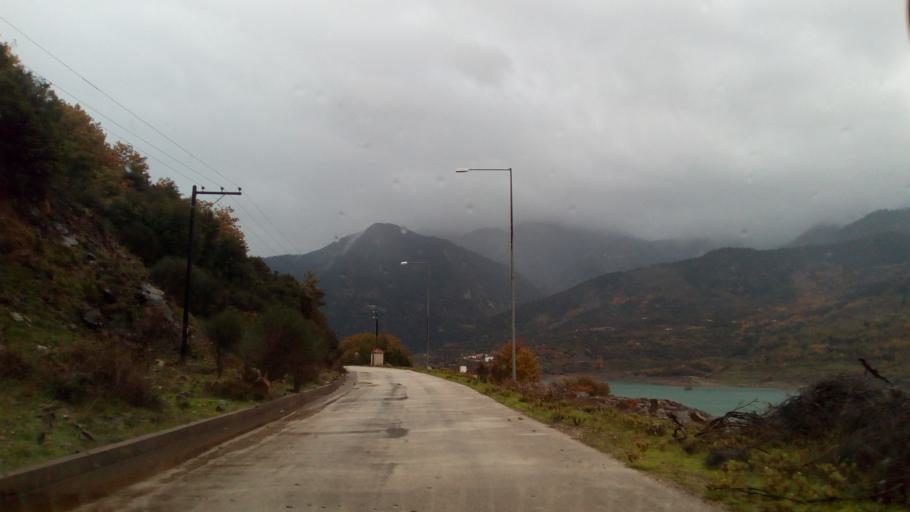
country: GR
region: West Greece
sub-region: Nomos Aitolias kai Akarnanias
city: Thermo
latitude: 38.6711
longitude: 21.8397
